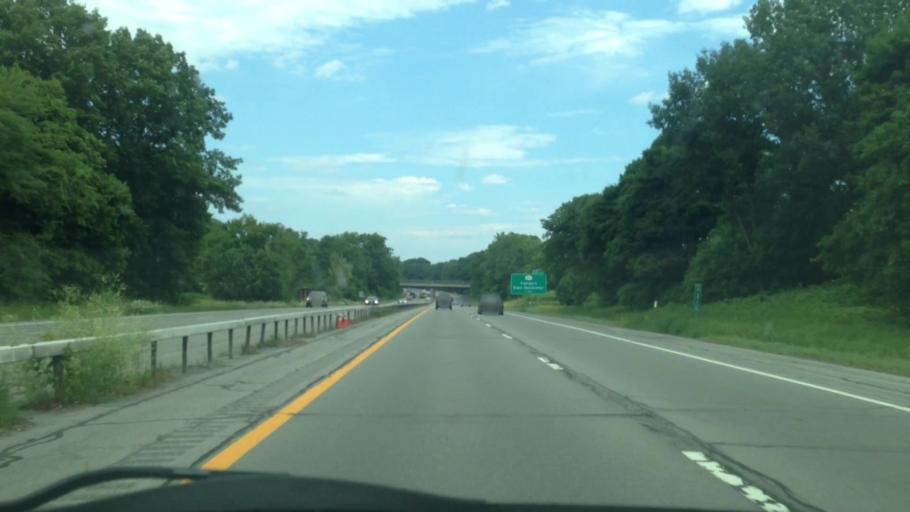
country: US
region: New York
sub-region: Monroe County
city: Pittsford
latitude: 43.0928
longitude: -77.5002
